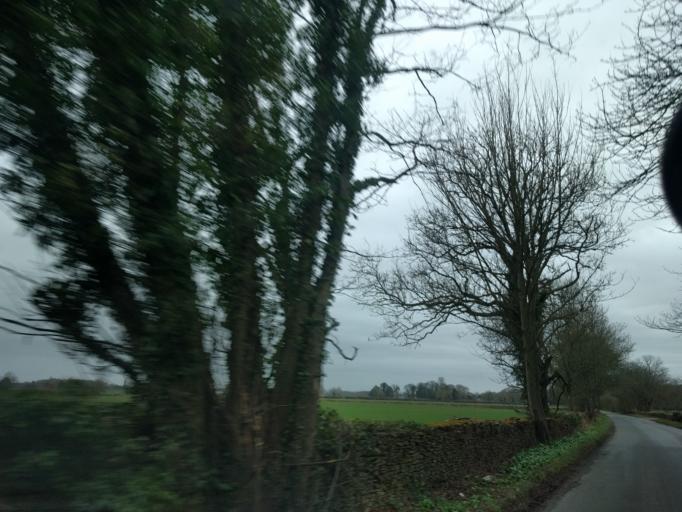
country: GB
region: England
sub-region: Gloucestershire
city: Tetbury
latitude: 51.6174
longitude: -2.2089
